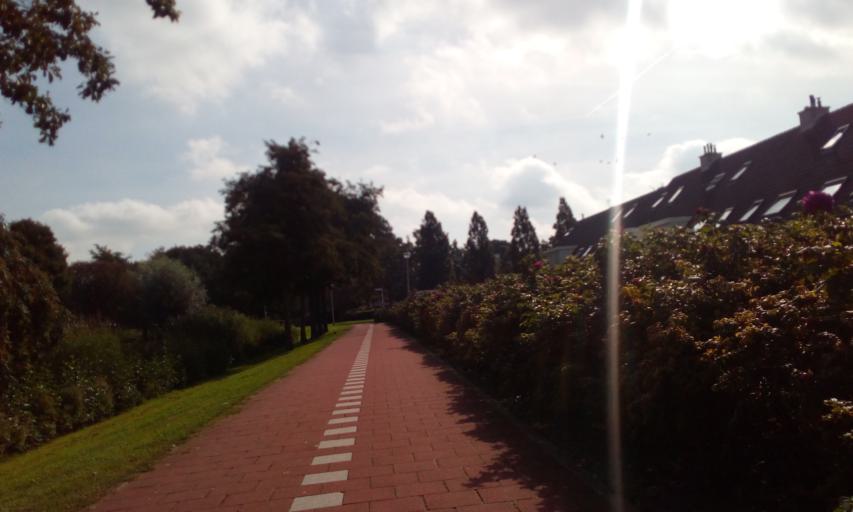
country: NL
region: South Holland
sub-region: Gemeente Katwijk
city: Katwijk aan den Rijn
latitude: 52.2099
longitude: 4.4152
